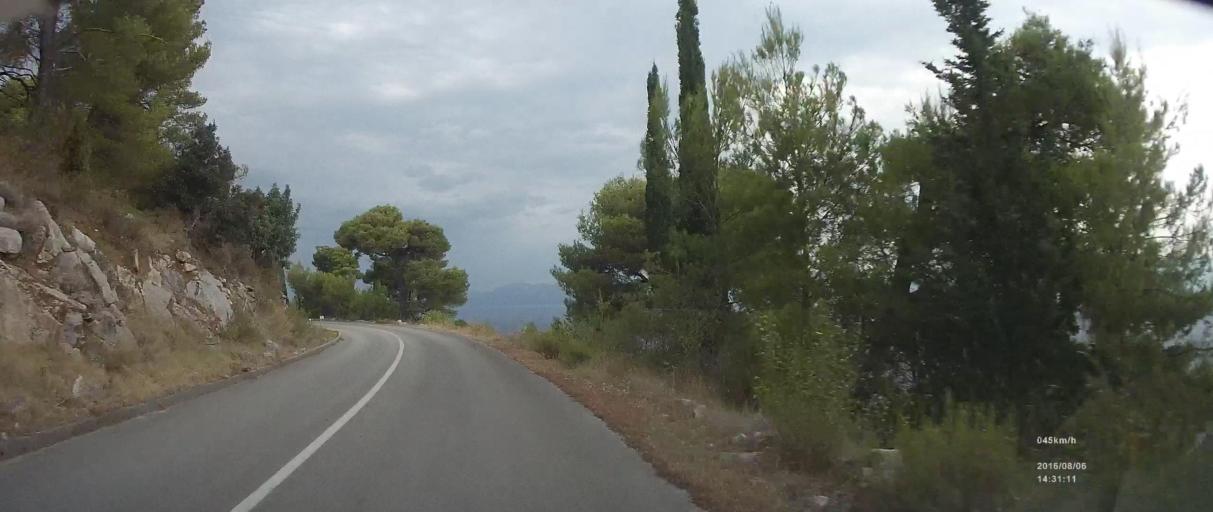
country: HR
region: Dubrovacko-Neretvanska
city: Ston
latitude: 42.7126
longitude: 17.7218
